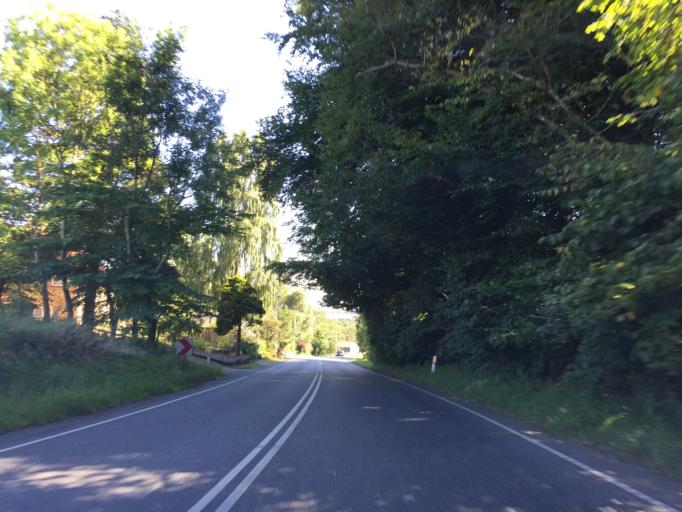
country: DK
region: Central Jutland
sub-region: Viborg Kommune
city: Bjerringbro
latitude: 56.3154
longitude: 9.6878
